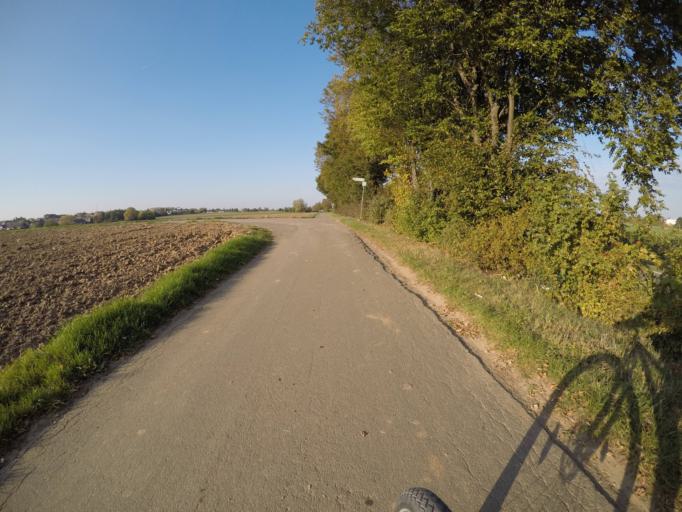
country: DE
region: Baden-Wuerttemberg
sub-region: Regierungsbezirk Stuttgart
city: Ostfildern
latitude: 48.7308
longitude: 9.2357
